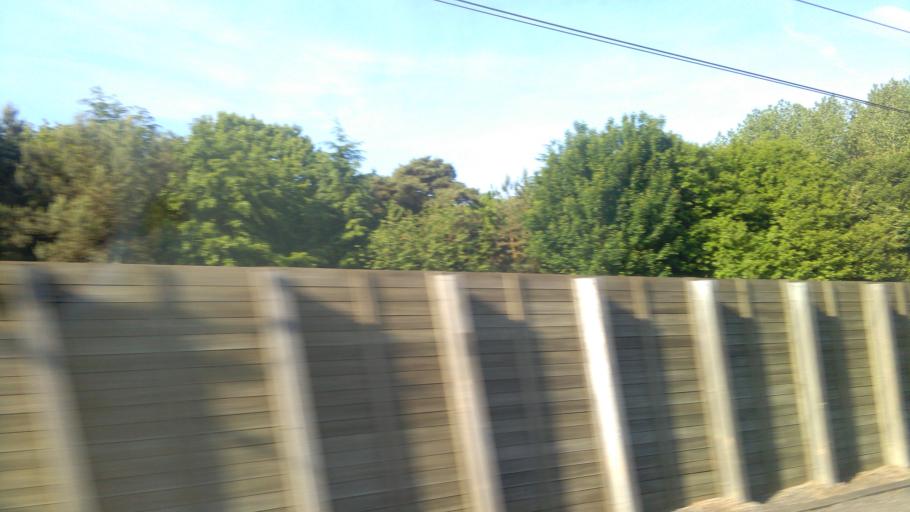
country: GB
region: England
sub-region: Kent
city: Hythe
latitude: 51.0915
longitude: 1.0604
